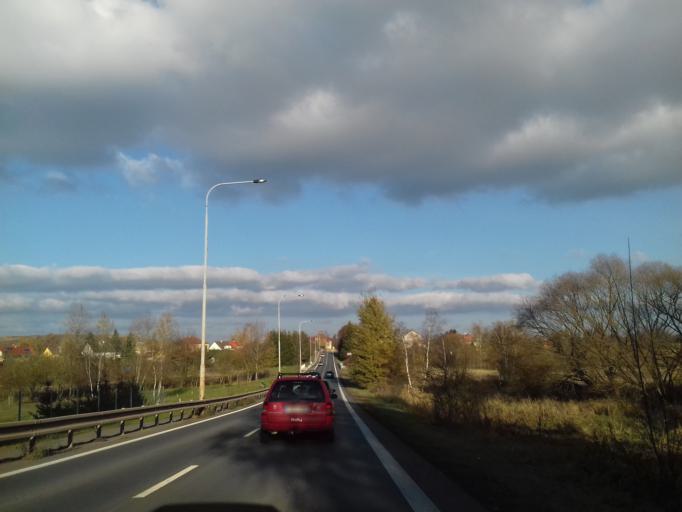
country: CZ
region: Plzensky
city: Zbuch
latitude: 49.6800
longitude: 13.2284
